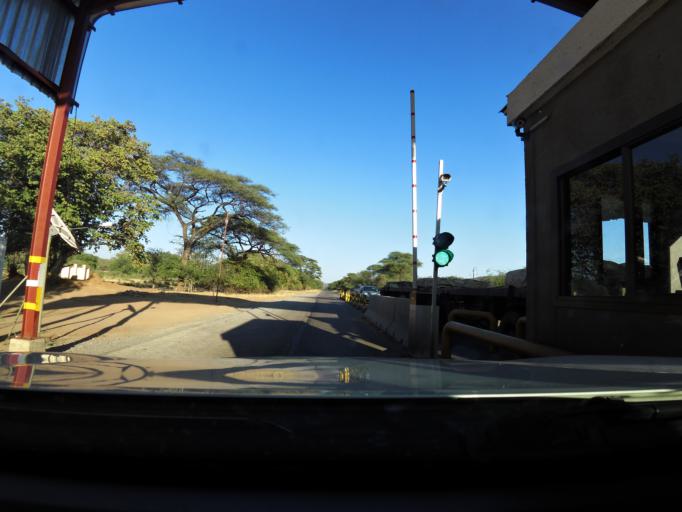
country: ZW
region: Matabeleland North
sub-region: Hwange District
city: Hwange
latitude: -18.3811
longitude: 26.7253
